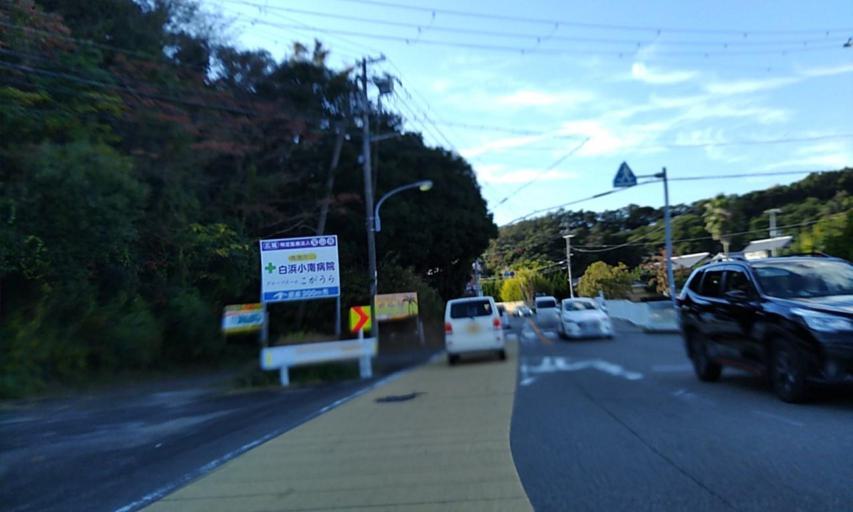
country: JP
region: Wakayama
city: Tanabe
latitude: 33.6799
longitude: 135.3590
